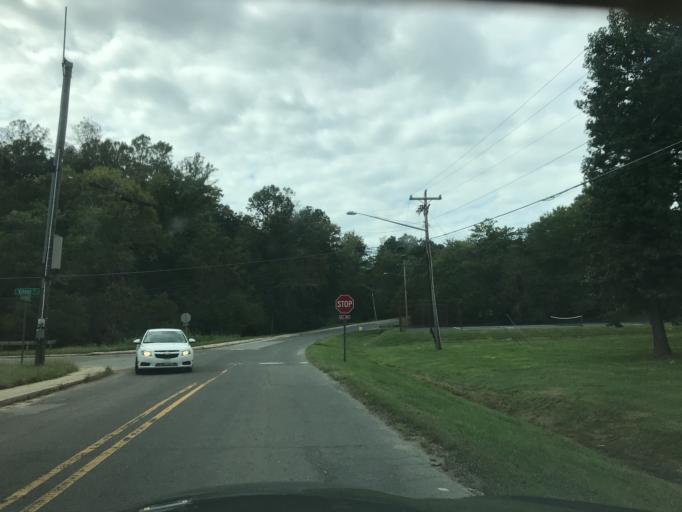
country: US
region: North Carolina
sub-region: Orange County
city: Chapel Hill
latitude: 35.9226
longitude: -79.0654
